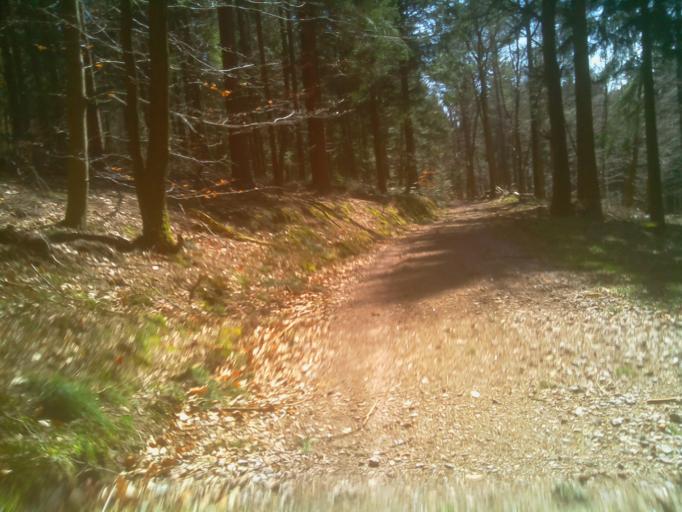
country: DE
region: Baden-Wuerttemberg
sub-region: Karlsruhe Region
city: Wilhelmsfeld
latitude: 49.4748
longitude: 8.7649
